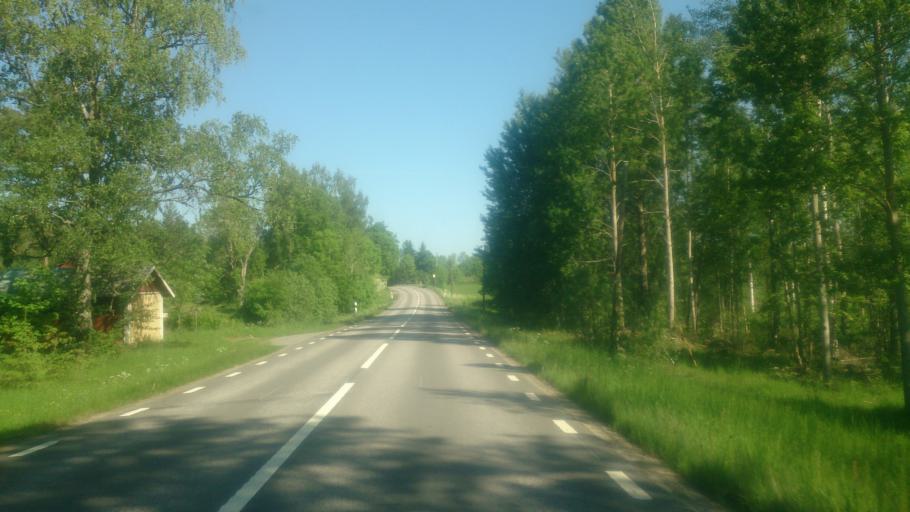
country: SE
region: OEstergoetland
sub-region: Atvidabergs Kommun
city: Atvidaberg
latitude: 58.1352
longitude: 16.0913
